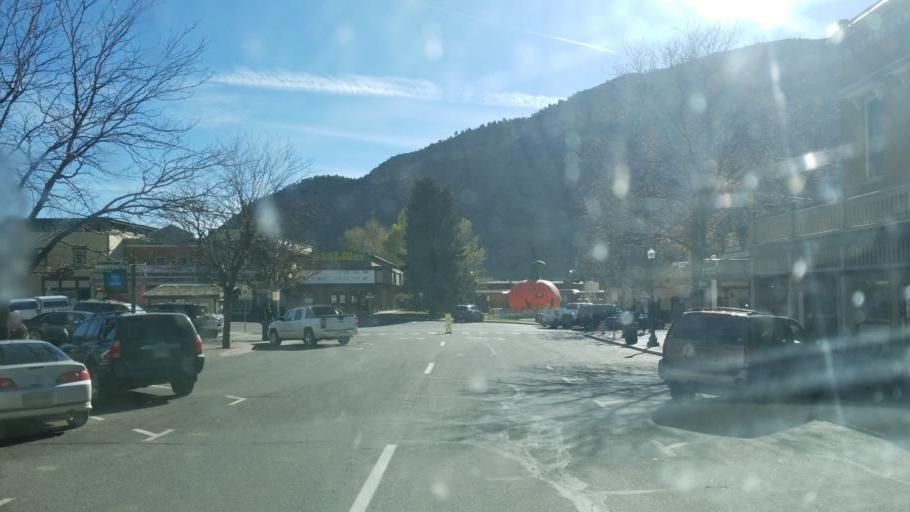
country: US
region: Colorado
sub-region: La Plata County
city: Durango
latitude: 37.2696
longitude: -107.8820
